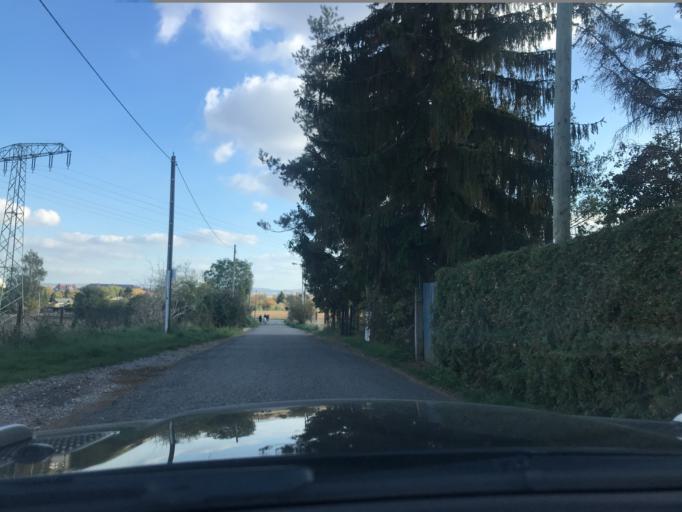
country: DE
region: Thuringia
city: Erfurt
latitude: 50.9850
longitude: 10.9959
